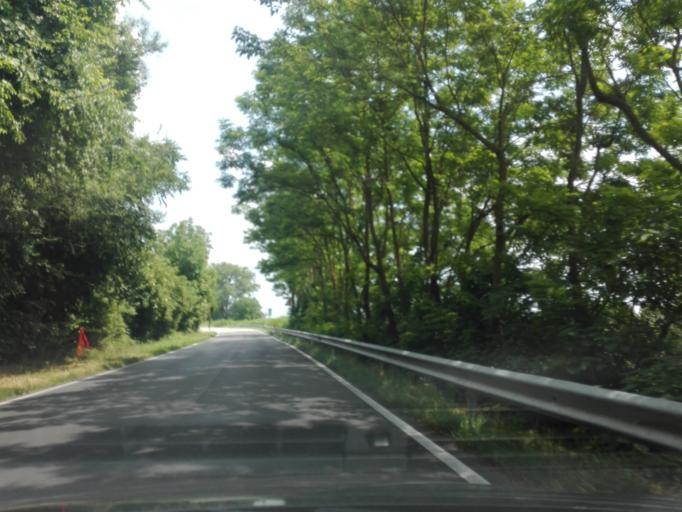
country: IT
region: Veneto
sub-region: Provincia di Rovigo
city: Adria
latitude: 45.0485
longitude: 12.0292
